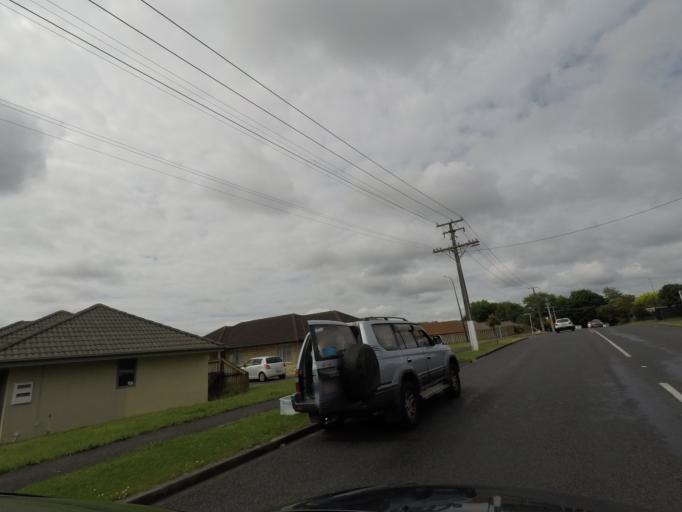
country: NZ
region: Auckland
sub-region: Auckland
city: Waitakere
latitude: -36.9021
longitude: 174.6217
